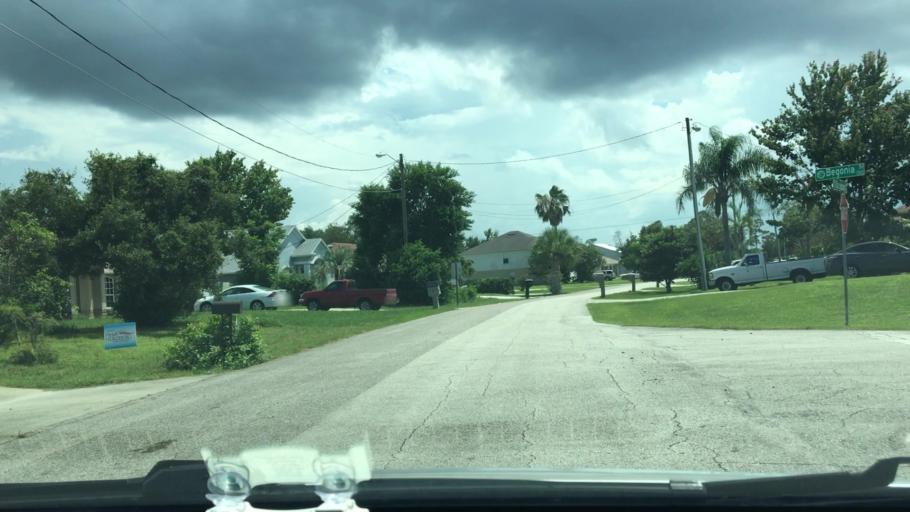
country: US
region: Florida
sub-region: Volusia County
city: Deltona
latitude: 28.8785
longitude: -81.2362
